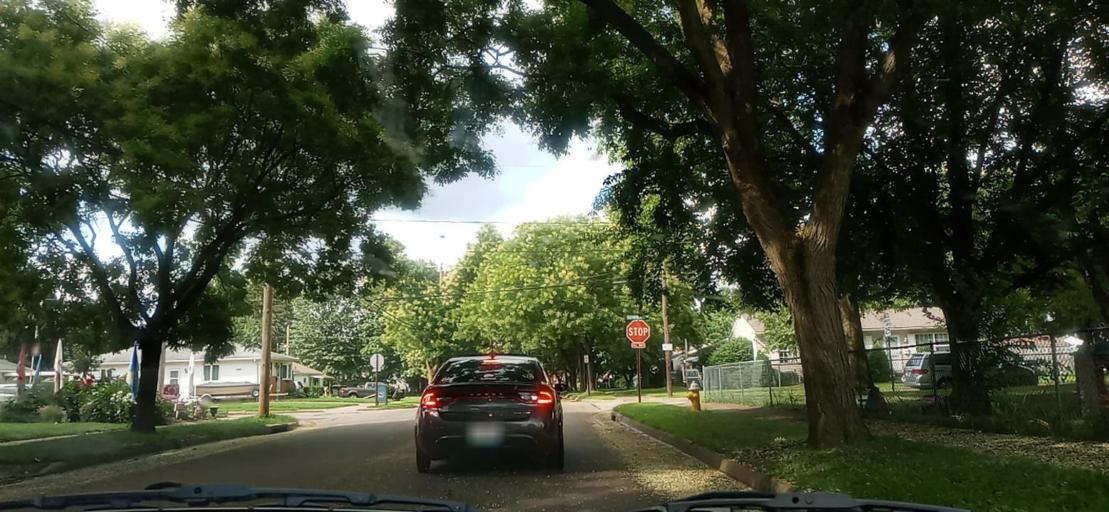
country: US
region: Ohio
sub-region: Summit County
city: Portage Lakes
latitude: 41.0261
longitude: -81.5634
